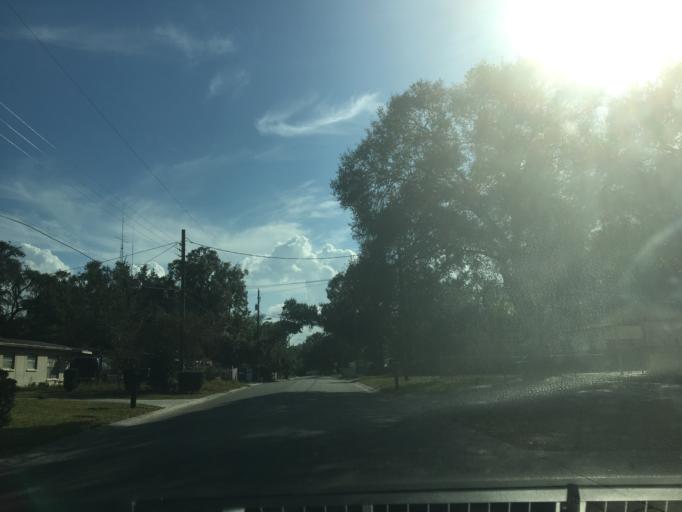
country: US
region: Florida
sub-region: Hillsborough County
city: University
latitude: 28.0429
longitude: -82.4330
